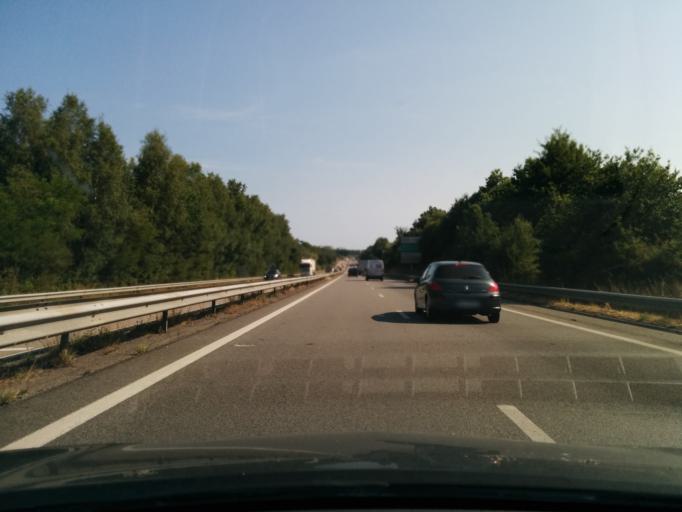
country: FR
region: Limousin
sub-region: Departement de la Haute-Vienne
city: Rilhac-Rancon
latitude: 45.9058
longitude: 1.2917
